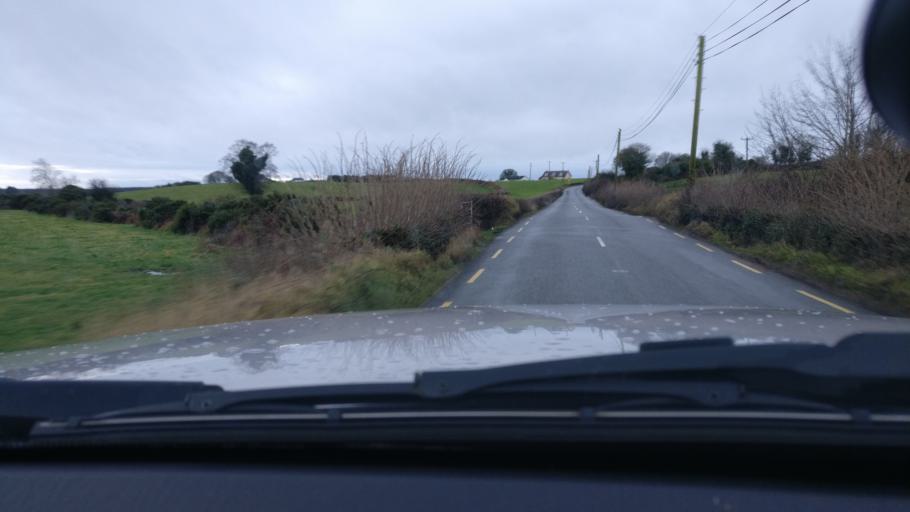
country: IE
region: Leinster
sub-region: An Longfort
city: Granard
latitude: 53.7951
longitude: -7.3923
